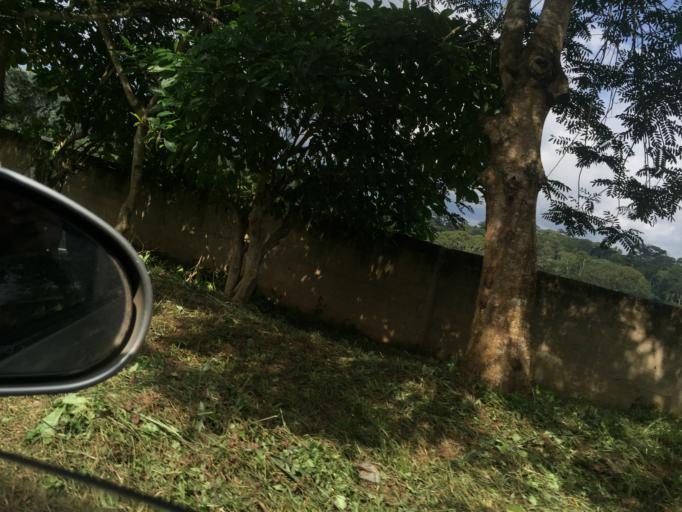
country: GH
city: Mpraeso
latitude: 6.6027
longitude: -0.7396
